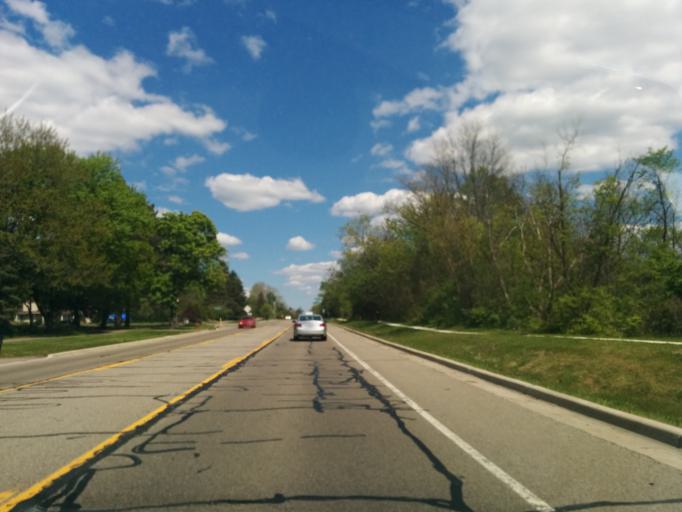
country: US
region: Michigan
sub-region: Oakland County
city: West Bloomfield Township
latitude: 42.5274
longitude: -83.3946
